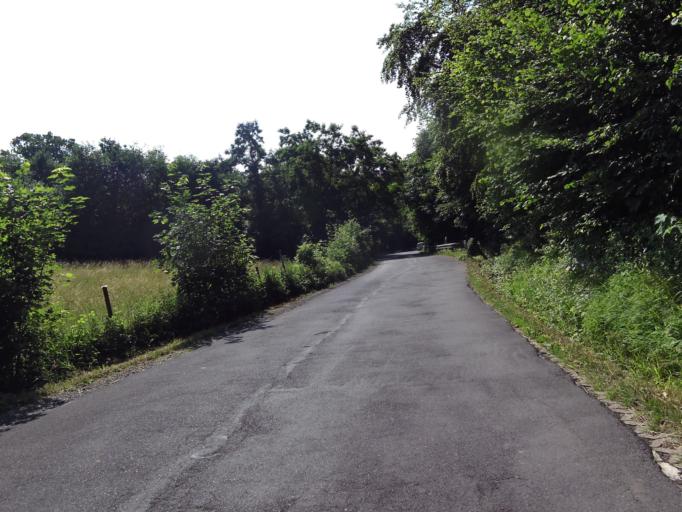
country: DE
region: Bavaria
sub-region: Regierungsbezirk Unterfranken
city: Hochberg
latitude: 49.7761
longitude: 9.9168
